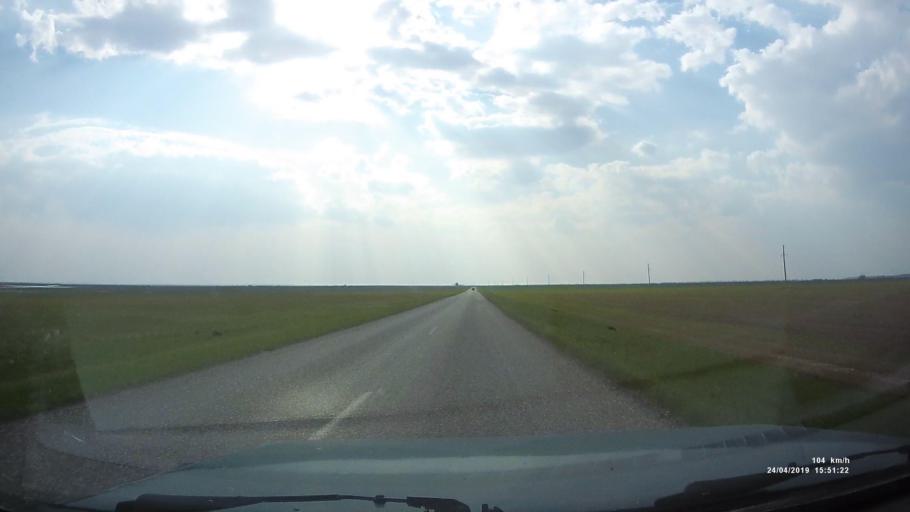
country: RU
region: Kalmykiya
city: Yashalta
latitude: 46.6044
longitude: 42.6122
